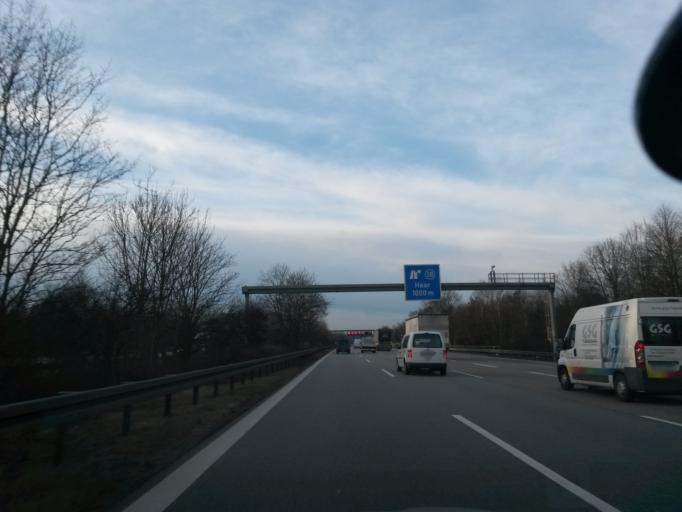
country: DE
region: Bavaria
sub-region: Upper Bavaria
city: Vaterstetten
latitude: 48.1207
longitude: 11.7582
